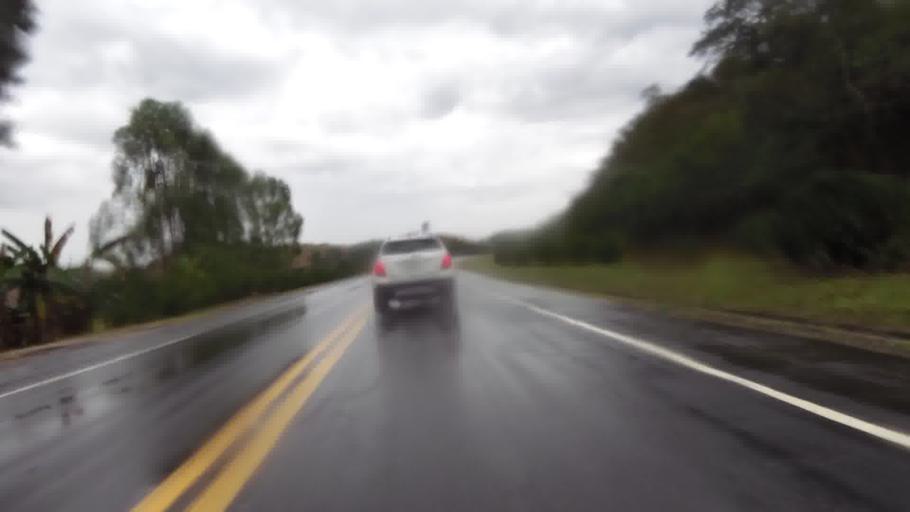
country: BR
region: Espirito Santo
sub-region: Cachoeiro De Itapemirim
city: Cachoeiro de Itapemirim
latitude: -21.0063
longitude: -41.1371
